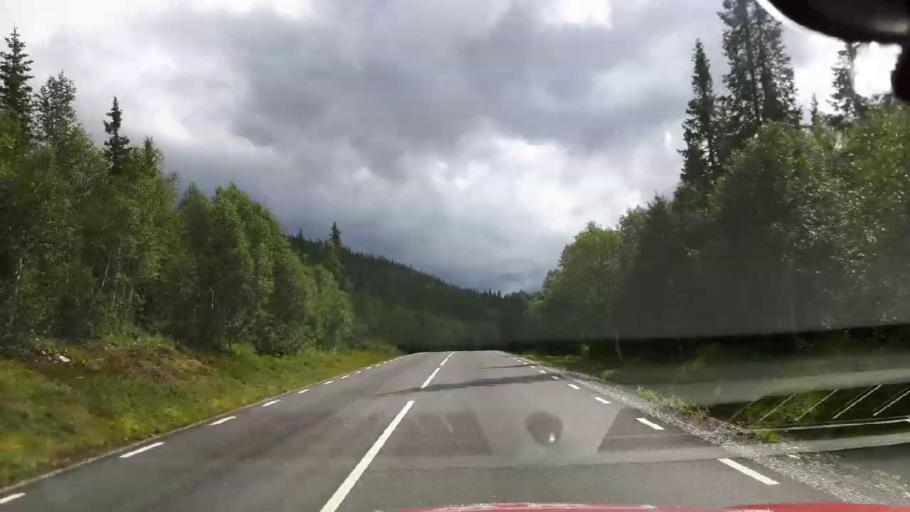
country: NO
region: Nord-Trondelag
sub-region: Royrvik
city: Royrvik
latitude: 64.8867
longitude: 14.1976
